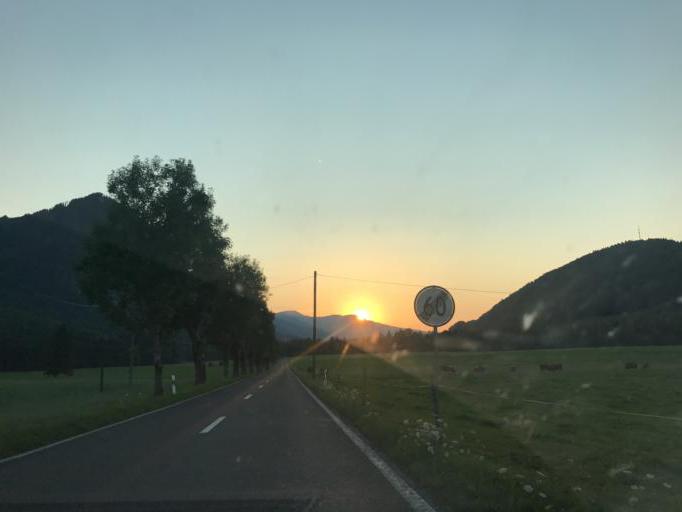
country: CH
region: Bern
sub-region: Frutigen-Niedersimmental District
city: Wimmis
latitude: 46.7013
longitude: 7.6051
